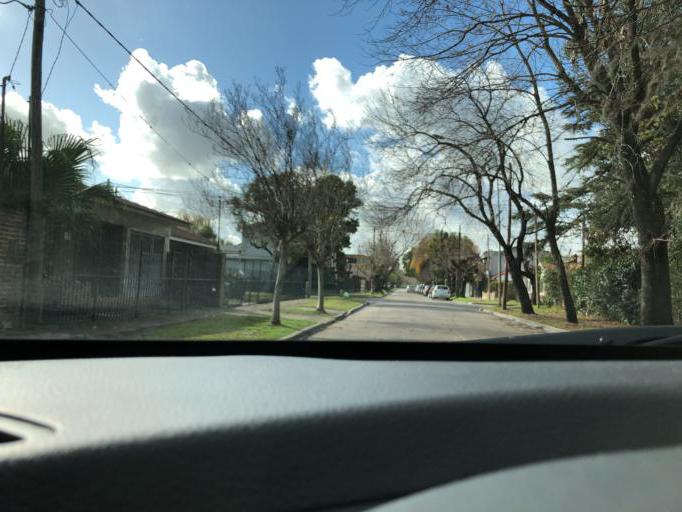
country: AR
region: Buenos Aires
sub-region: Partido de La Plata
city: La Plata
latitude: -34.8735
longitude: -58.0462
